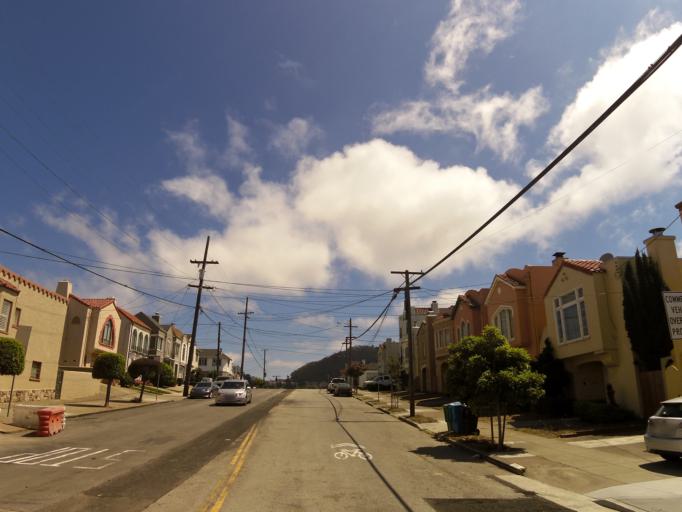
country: US
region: California
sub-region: San Mateo County
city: Daly City
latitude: 37.7394
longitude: -122.4733
